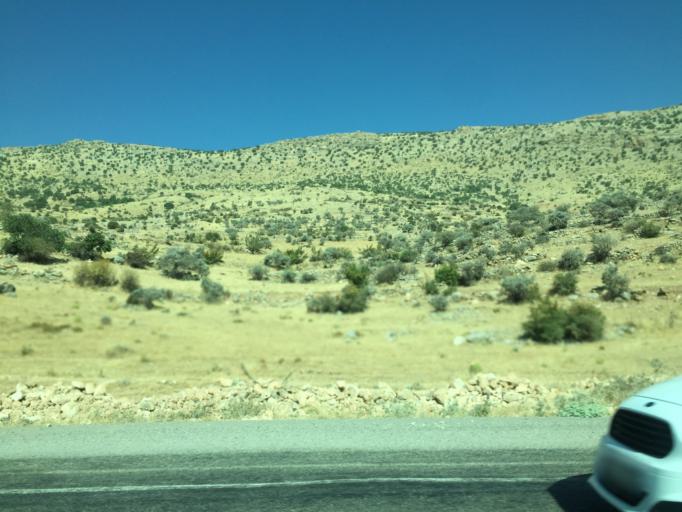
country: TR
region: Batman
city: Hasankeyf
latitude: 37.6845
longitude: 41.4529
